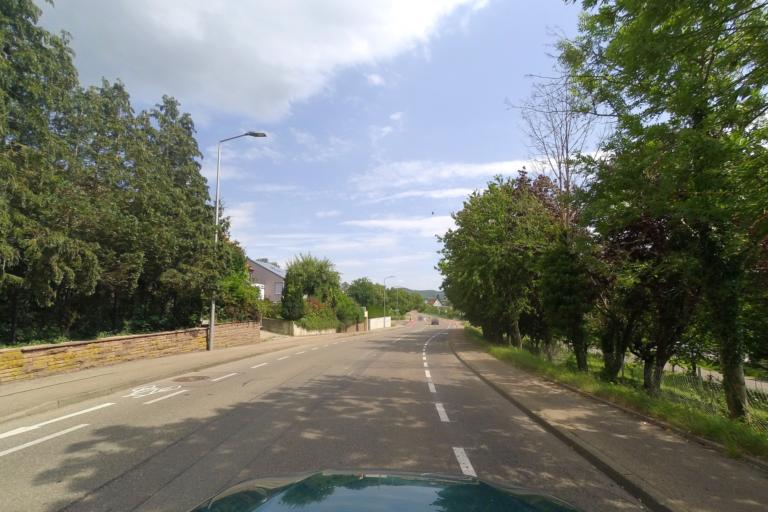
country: DE
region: Baden-Wuerttemberg
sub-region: Regierungsbezirk Stuttgart
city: Aalen
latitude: 48.8329
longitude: 10.1060
